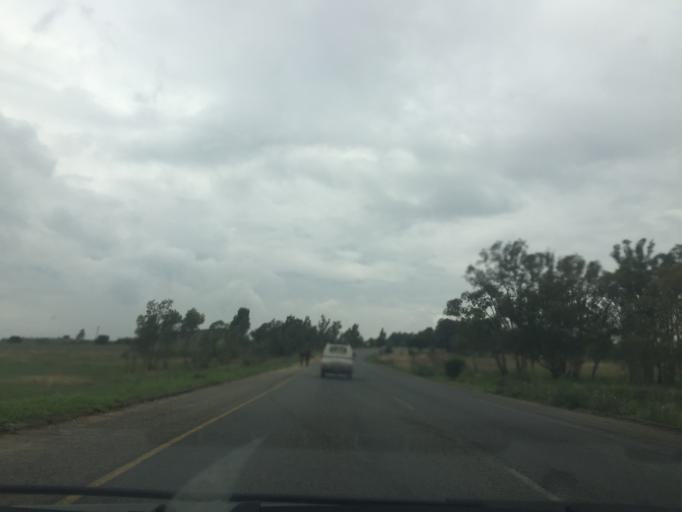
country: ZA
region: Gauteng
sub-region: City of Johannesburg Metropolitan Municipality
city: Diepsloot
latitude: -25.9669
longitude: 27.9346
